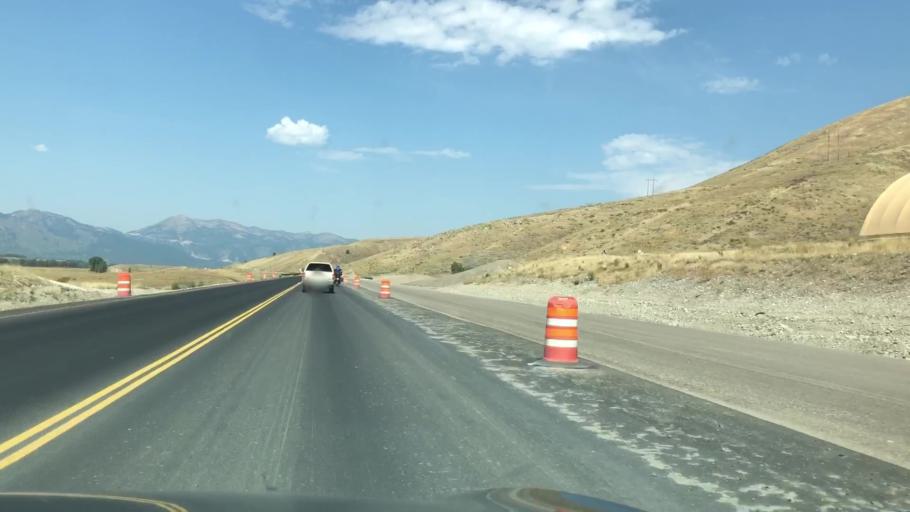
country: US
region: Wyoming
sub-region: Teton County
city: South Park
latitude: 43.4018
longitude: -110.7547
